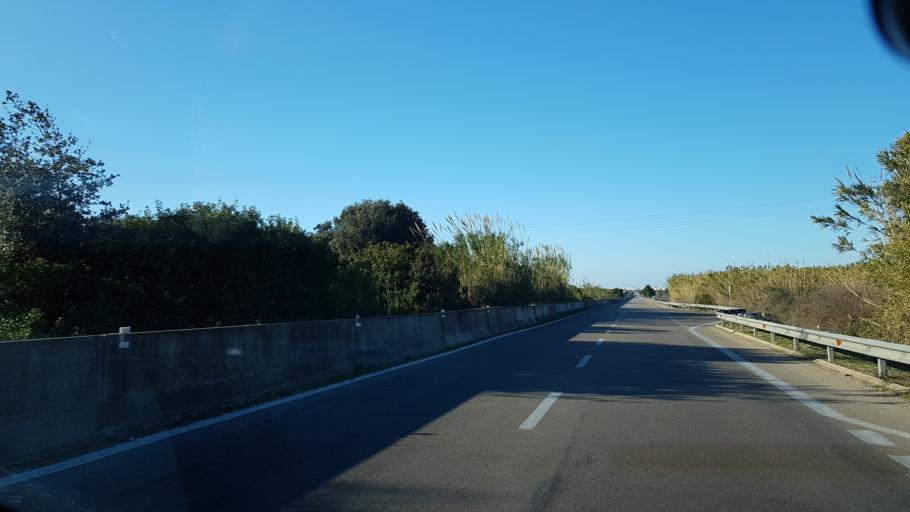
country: IT
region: Apulia
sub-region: Provincia di Lecce
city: Alezio
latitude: 40.0167
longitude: 18.0465
